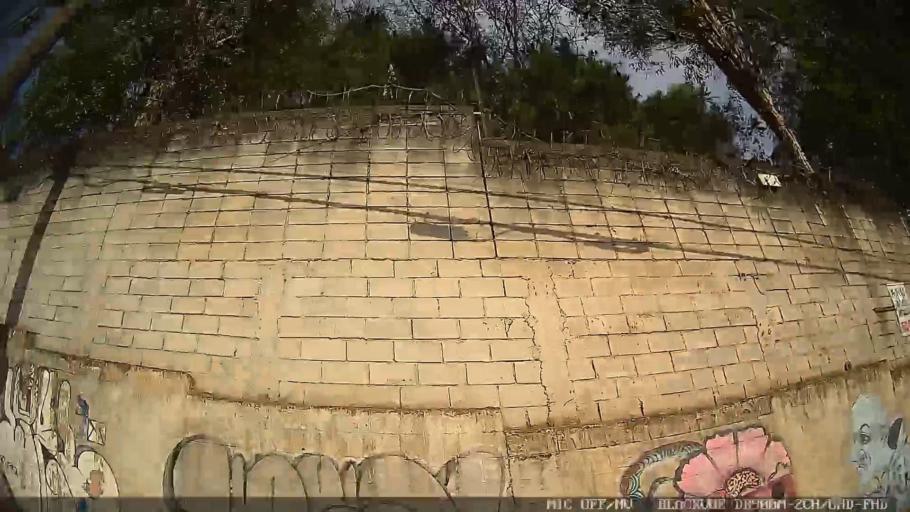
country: BR
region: Sao Paulo
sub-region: Taboao Da Serra
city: Taboao da Serra
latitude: -23.6138
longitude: -46.7554
